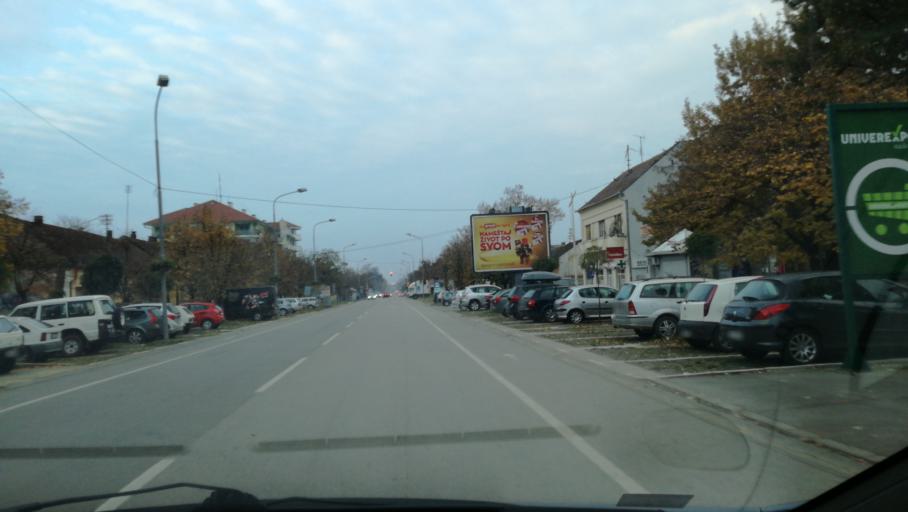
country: RS
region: Autonomna Pokrajina Vojvodina
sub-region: Severnobanatski Okrug
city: Kikinda
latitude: 45.8279
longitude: 20.4620
